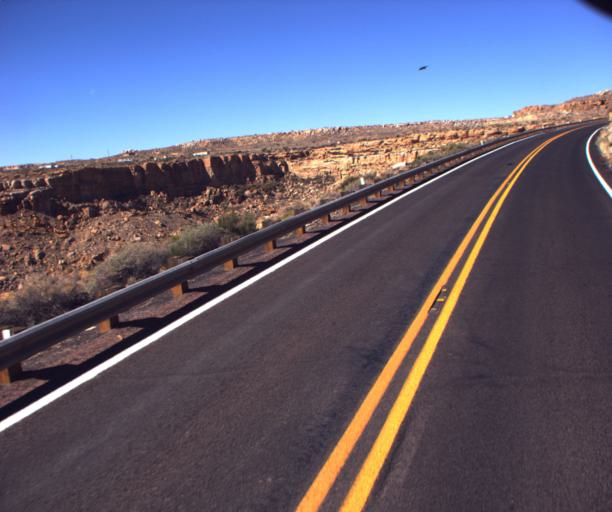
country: US
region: Arizona
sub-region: Navajo County
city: First Mesa
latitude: 35.8824
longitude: -110.6276
